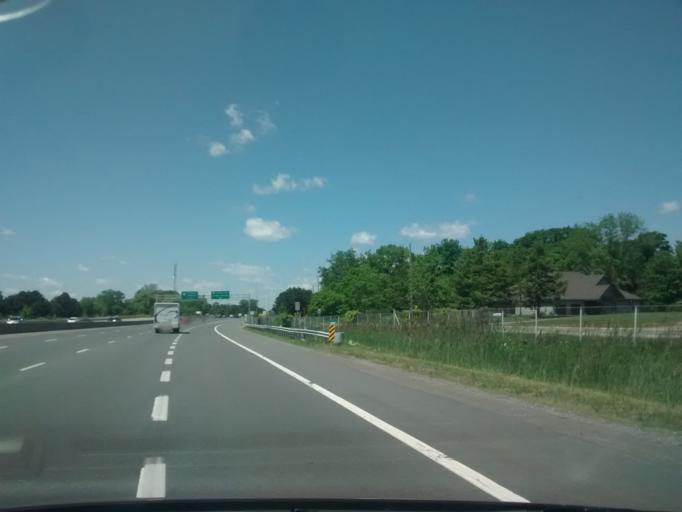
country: CA
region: Ontario
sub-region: Regional Municipality of Niagara
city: St. Catharines
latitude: 43.1794
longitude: -79.3535
